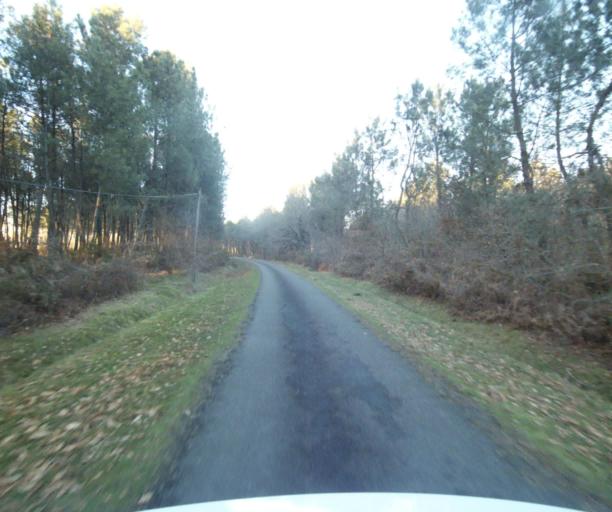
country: FR
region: Aquitaine
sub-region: Departement des Landes
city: Gabarret
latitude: 44.0953
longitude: -0.0285
